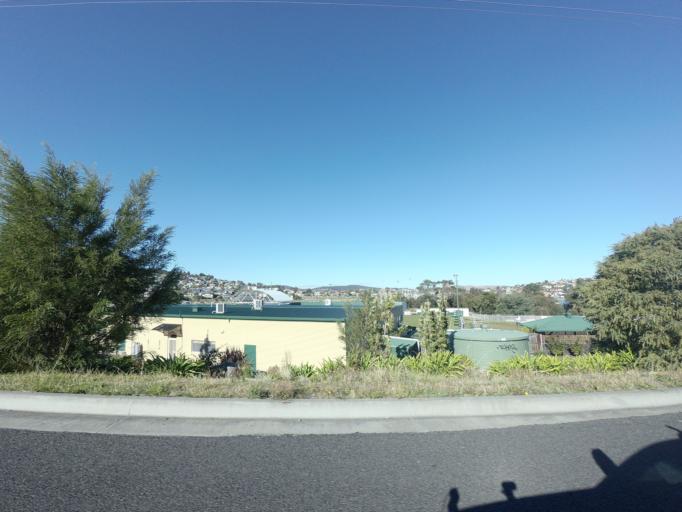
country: AU
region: Tasmania
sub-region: Clarence
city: Bellerive
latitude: -42.8704
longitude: 147.3629
